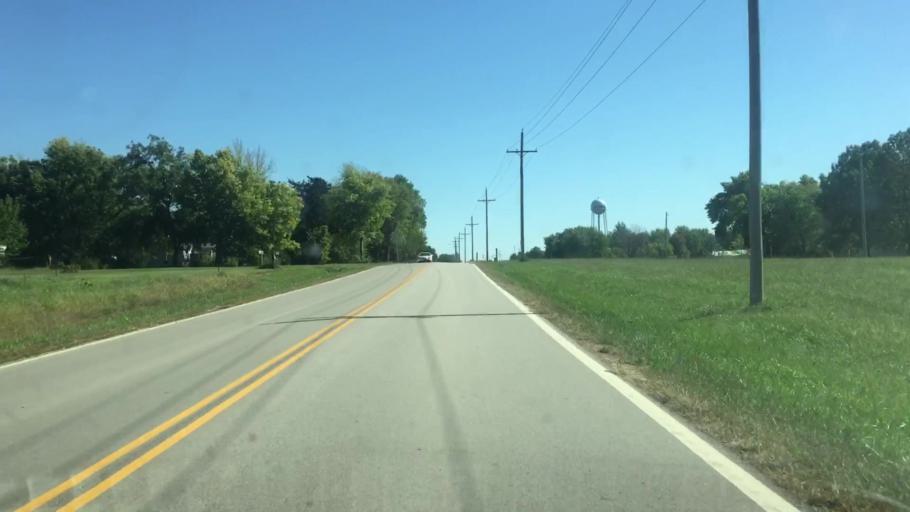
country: US
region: Kansas
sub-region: Jackson County
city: Holton
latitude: 39.6063
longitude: -95.7212
